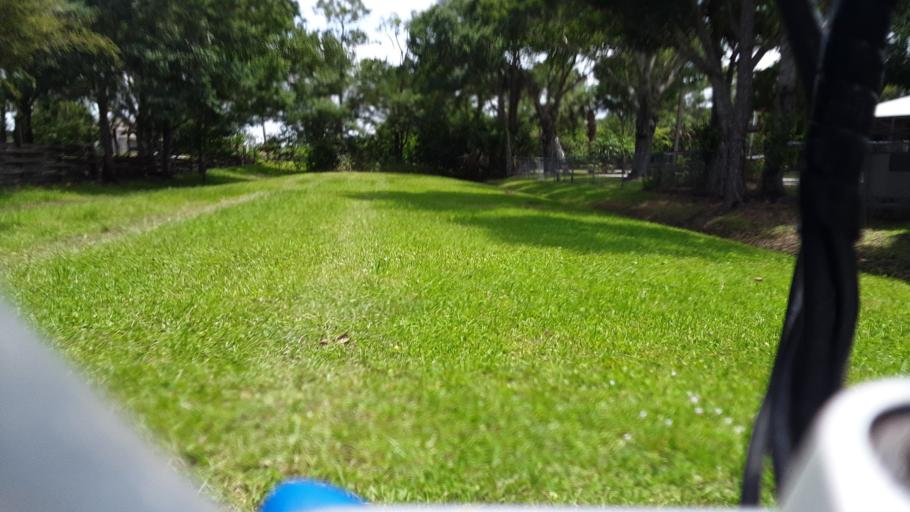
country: US
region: Florida
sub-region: Brevard County
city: Malabar
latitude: 27.9843
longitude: -80.6019
